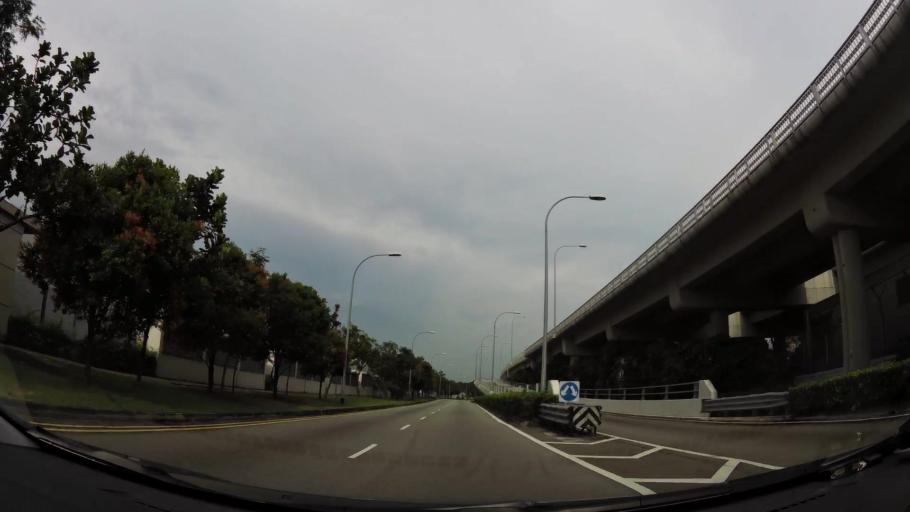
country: SG
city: Singapore
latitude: 1.3419
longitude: 103.8875
